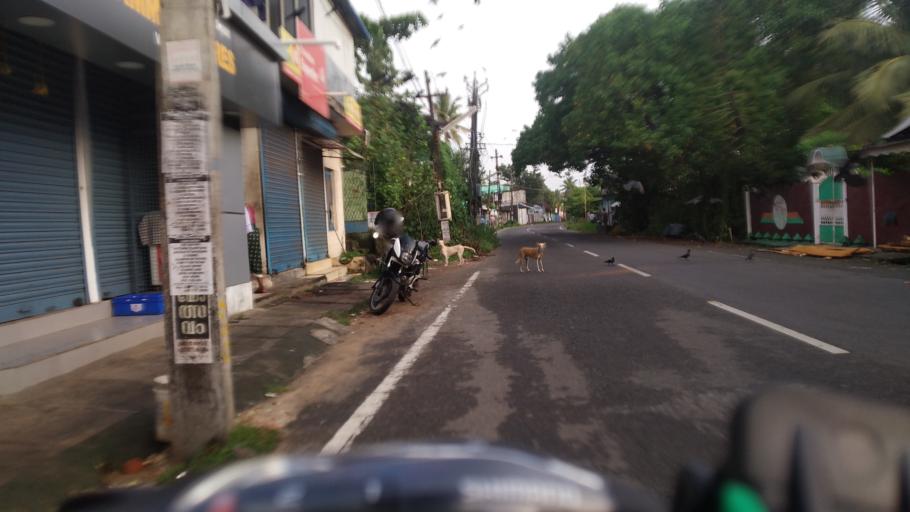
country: IN
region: Kerala
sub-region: Ernakulam
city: Cochin
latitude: 9.9775
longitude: 76.2411
